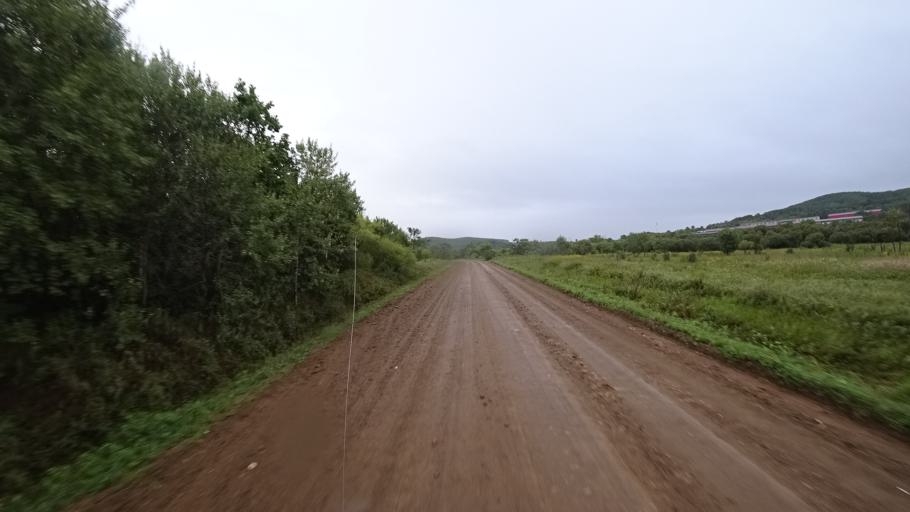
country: RU
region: Primorskiy
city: Monastyrishche
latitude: 44.2739
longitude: 132.4613
